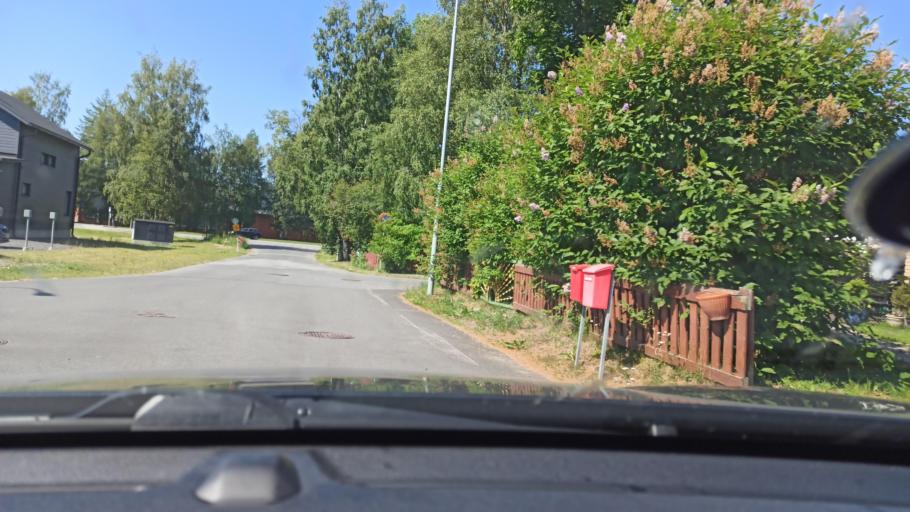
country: FI
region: Northern Ostrobothnia
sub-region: Oulu
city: Oulu
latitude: 65.0411
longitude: 25.4419
